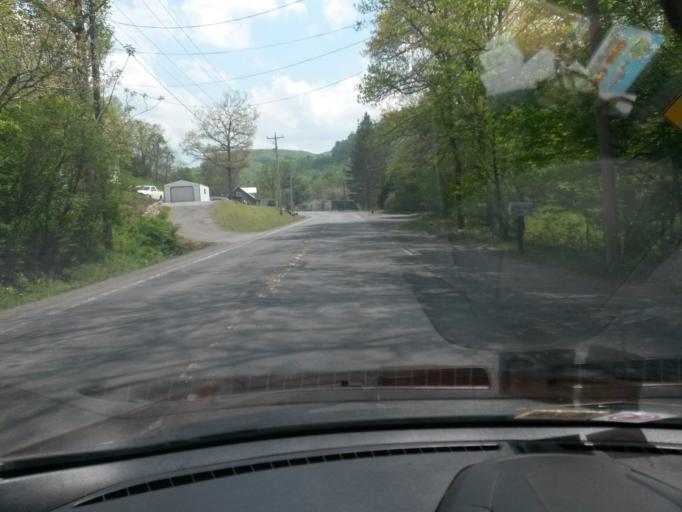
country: US
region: West Virginia
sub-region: Greenbrier County
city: Rainelle
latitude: 37.9917
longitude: -80.7337
